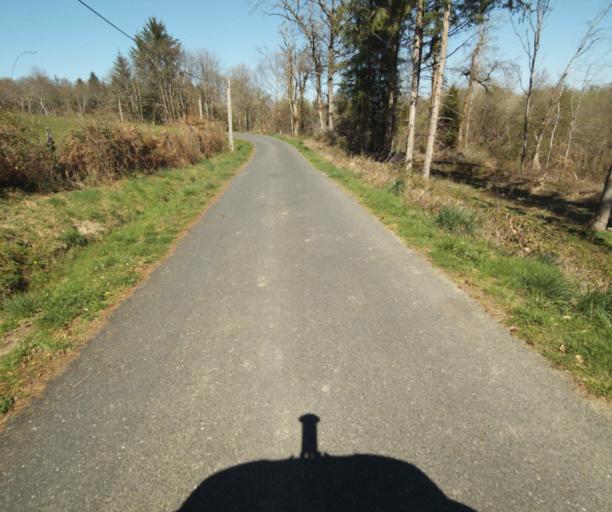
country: FR
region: Limousin
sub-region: Departement de la Correze
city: Saint-Mexant
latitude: 45.2899
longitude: 1.7005
